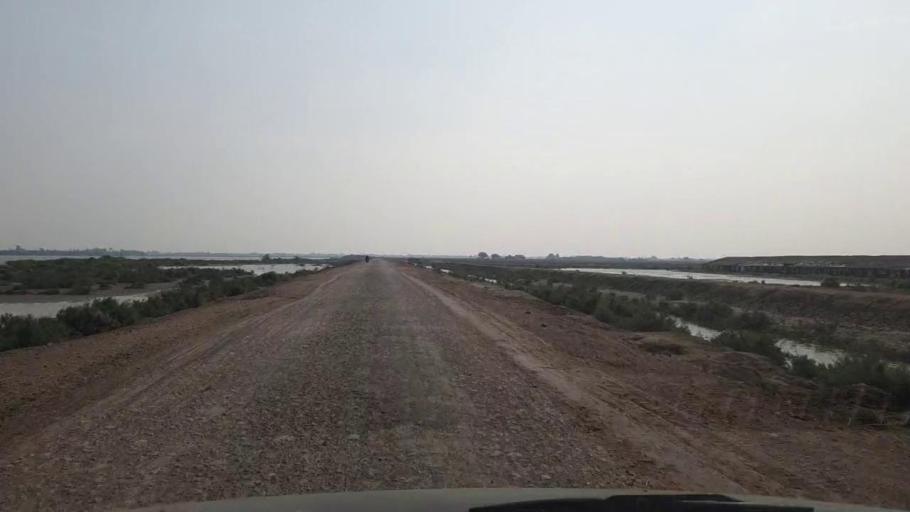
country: PK
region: Sindh
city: Tando Muhammad Khan
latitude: 25.0875
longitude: 68.3855
